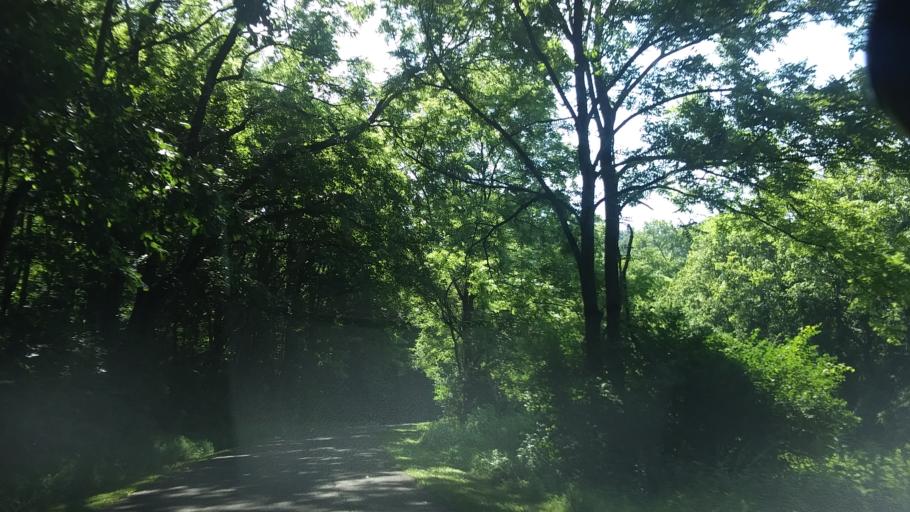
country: US
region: Tennessee
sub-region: Davidson County
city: Belle Meade
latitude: 36.0646
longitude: -86.8936
